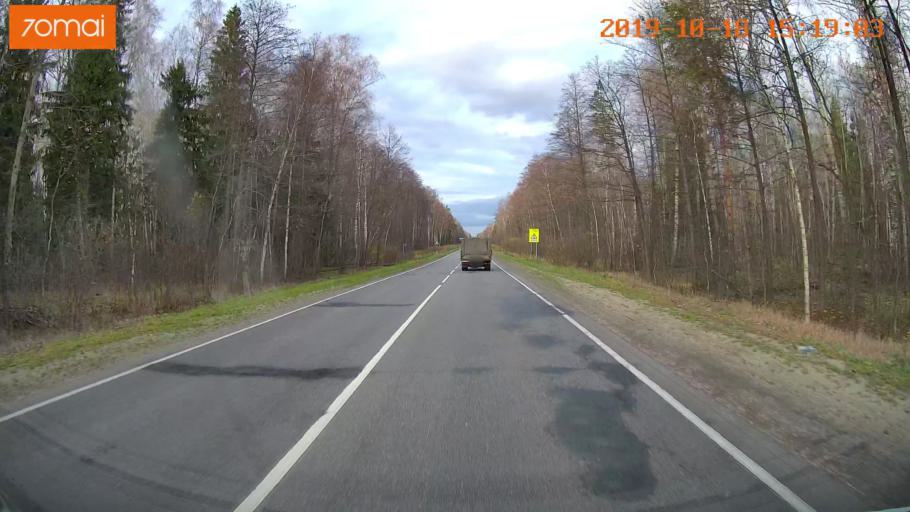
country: RU
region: Vladimir
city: Anopino
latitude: 55.6675
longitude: 40.7348
